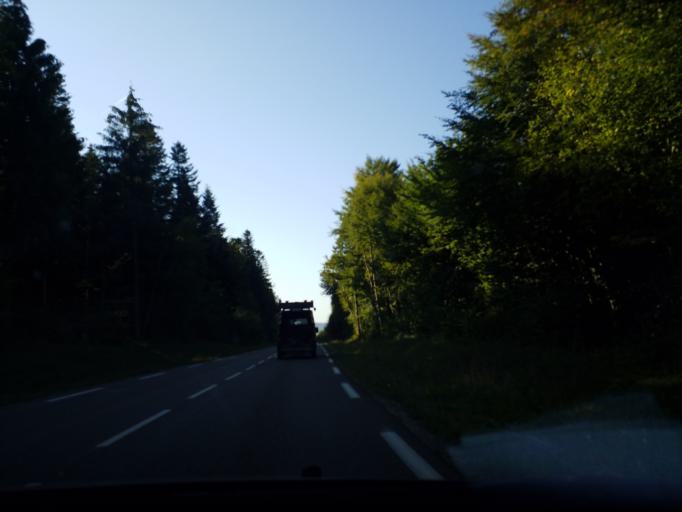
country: FR
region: Franche-Comte
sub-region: Departement du Doubs
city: Vercel-Villedieu-le-Camp
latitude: 47.2035
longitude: 6.3950
